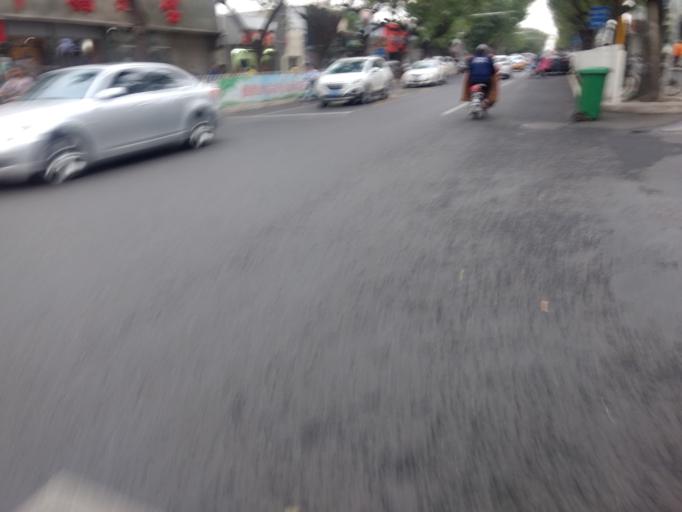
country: CN
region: Beijing
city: Jinrongjie
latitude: 39.9371
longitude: 116.3666
